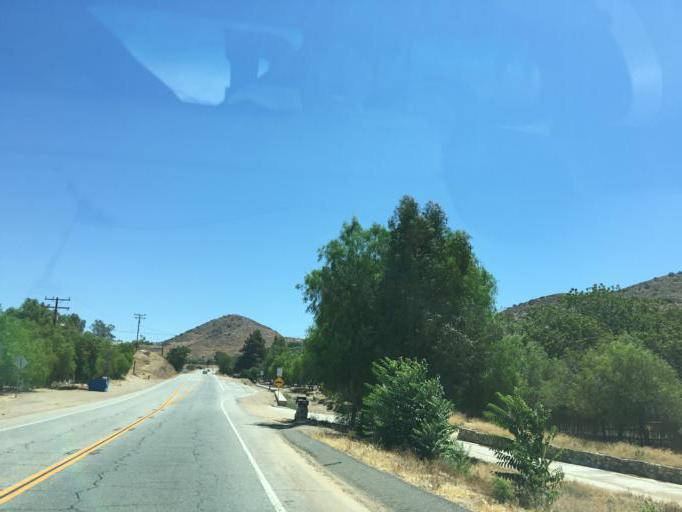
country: US
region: California
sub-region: Los Angeles County
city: Agua Dulce
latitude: 34.5199
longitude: -118.2883
